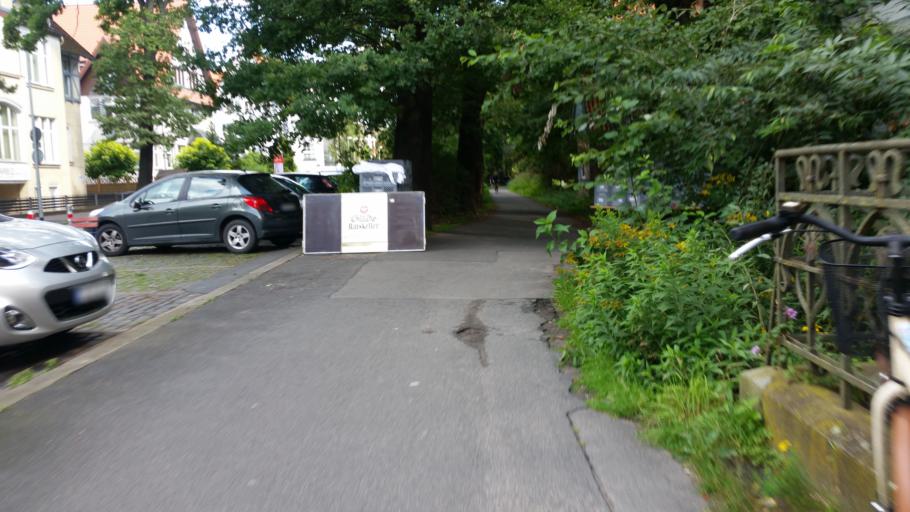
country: DE
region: Lower Saxony
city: Hannover
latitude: 52.3899
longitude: 9.7554
